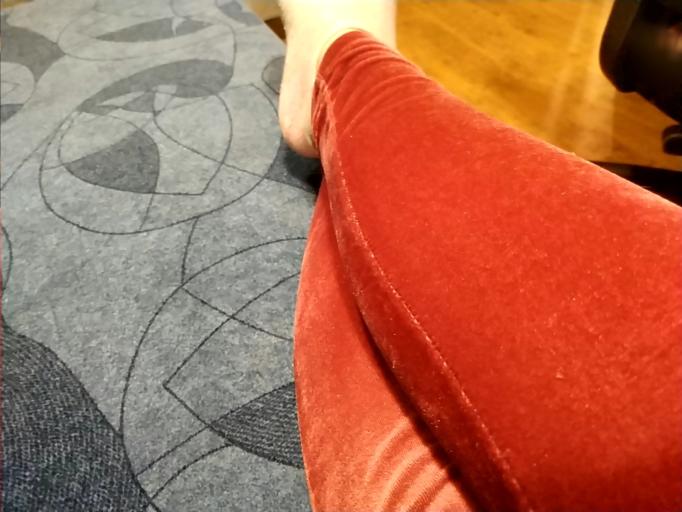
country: RU
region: Novgorod
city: Kulotino
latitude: 58.4062
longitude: 33.4489
